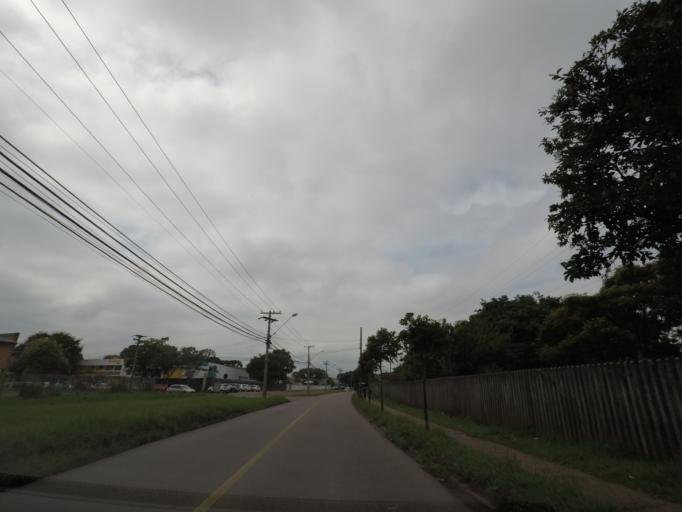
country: BR
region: Parana
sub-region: Curitiba
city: Curitiba
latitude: -25.4937
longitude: -49.3323
